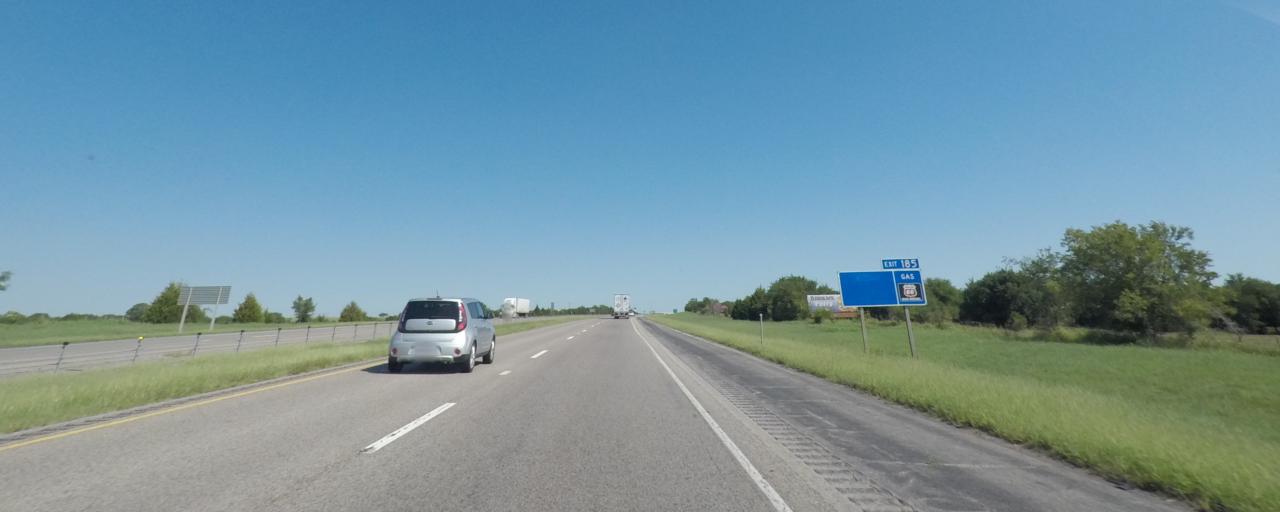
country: US
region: Oklahoma
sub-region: Noble County
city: Perry
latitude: 36.2622
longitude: -97.3269
